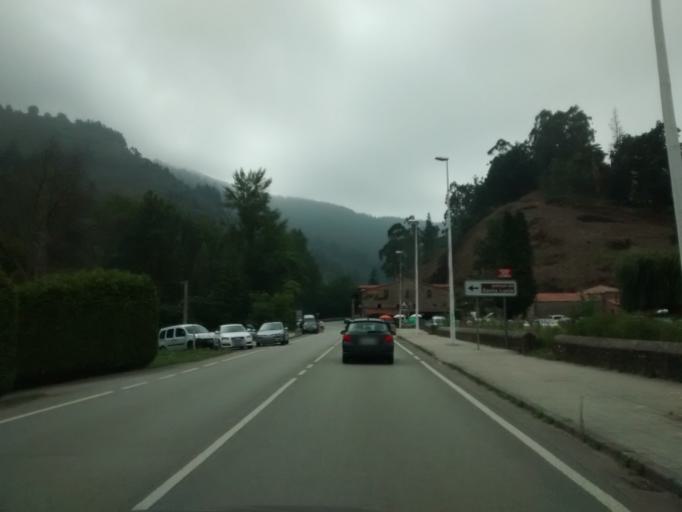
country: ES
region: Cantabria
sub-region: Provincia de Cantabria
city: Cabezon de la Sal
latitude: 43.2864
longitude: -4.2361
